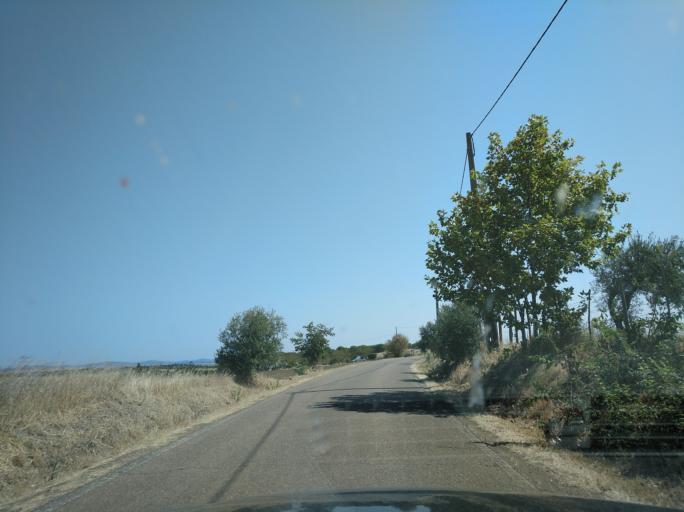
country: PT
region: Portalegre
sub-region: Campo Maior
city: Campo Maior
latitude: 39.0232
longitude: -7.0465
